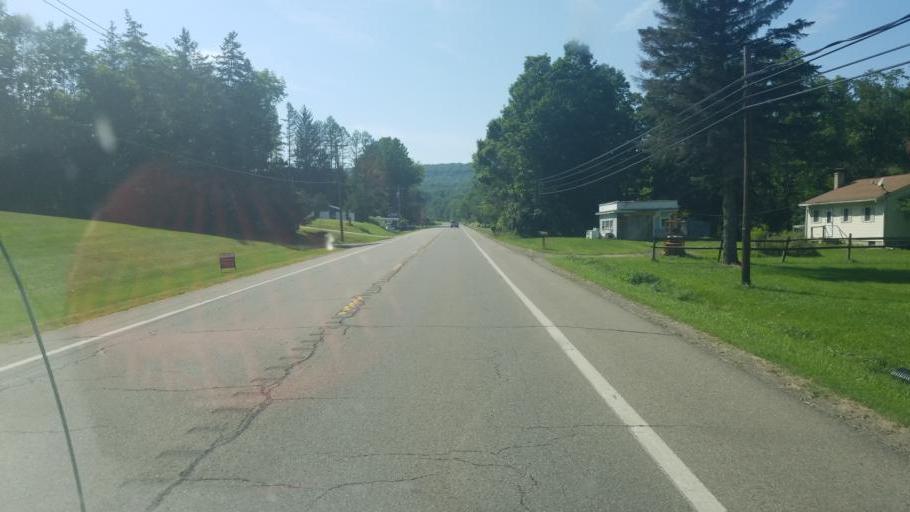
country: US
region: New York
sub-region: Allegany County
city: Wellsville
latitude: 42.1241
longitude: -77.9830
